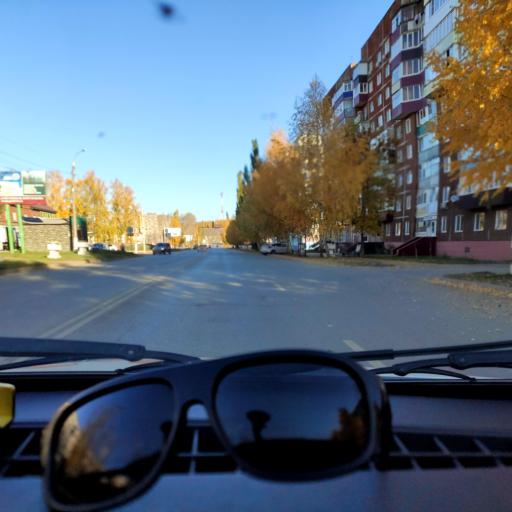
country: RU
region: Bashkortostan
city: Blagoveshchensk
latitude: 55.0505
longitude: 55.9540
